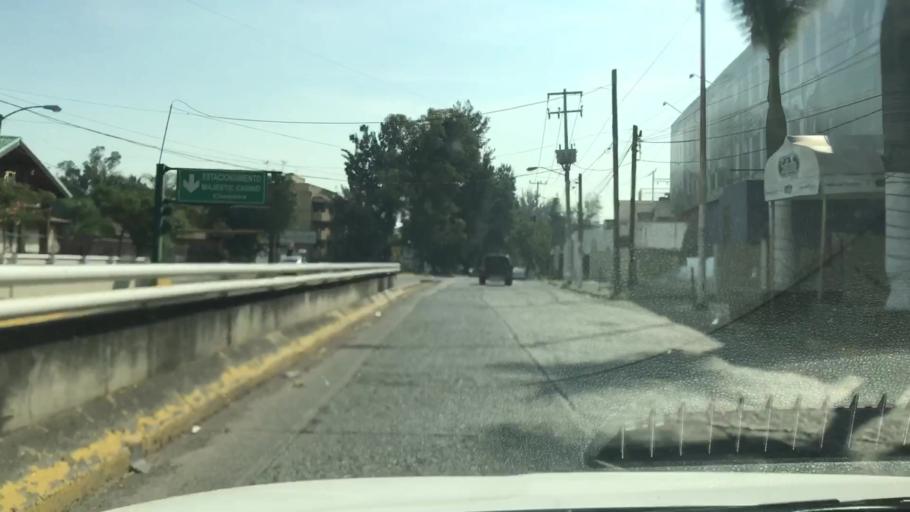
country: MX
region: Jalisco
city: Guadalajara
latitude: 20.6461
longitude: -103.4045
